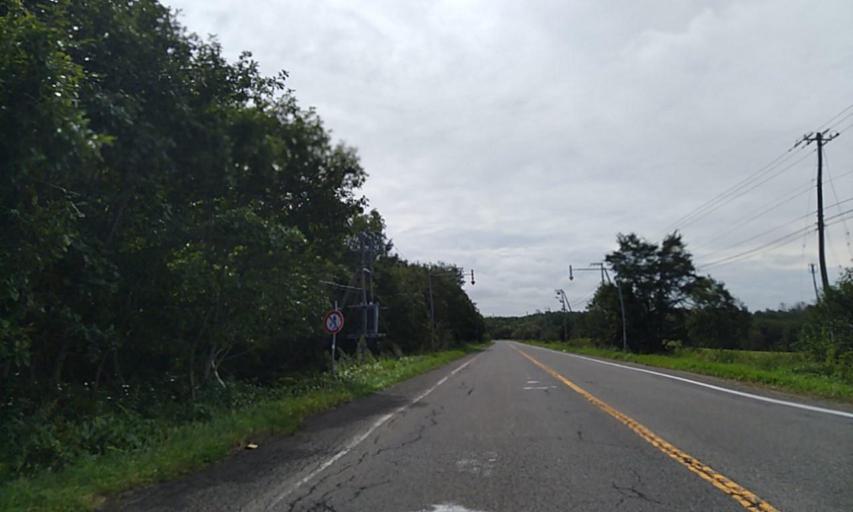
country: JP
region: Hokkaido
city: Shibetsu
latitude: 43.6177
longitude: 145.1799
